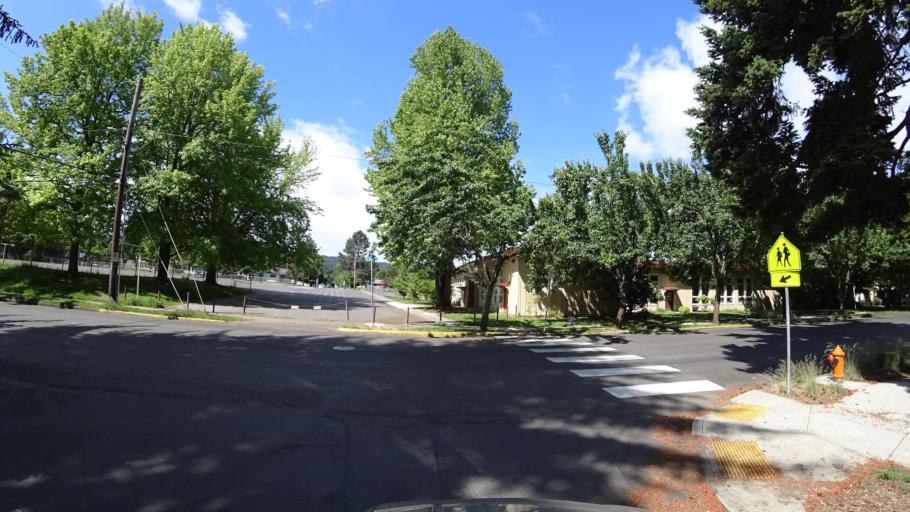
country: US
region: Oregon
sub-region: Washington County
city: West Haven
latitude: 45.5998
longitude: -122.7573
